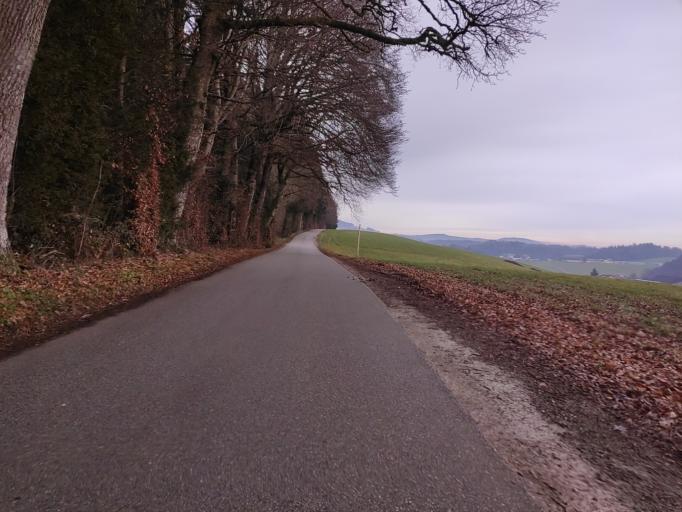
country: AT
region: Salzburg
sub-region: Politischer Bezirk Salzburg-Umgebung
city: Obertrum am See
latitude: 47.9065
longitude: 13.0649
